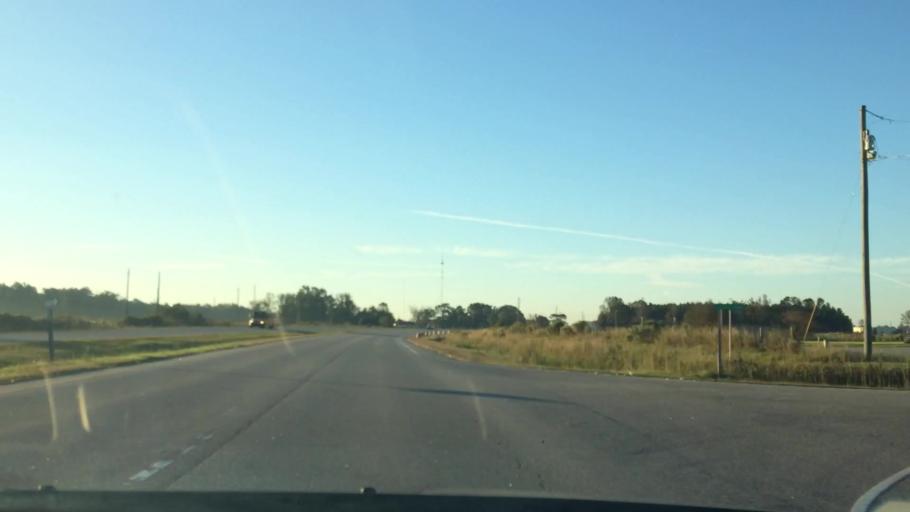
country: US
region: North Carolina
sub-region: Pitt County
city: Ayden
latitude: 35.4536
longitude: -77.4308
